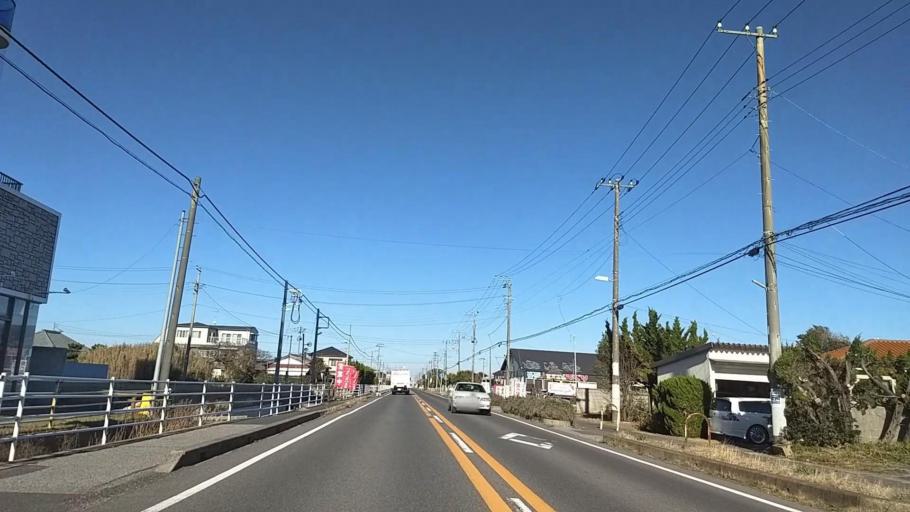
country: JP
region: Chiba
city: Togane
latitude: 35.4876
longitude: 140.4214
